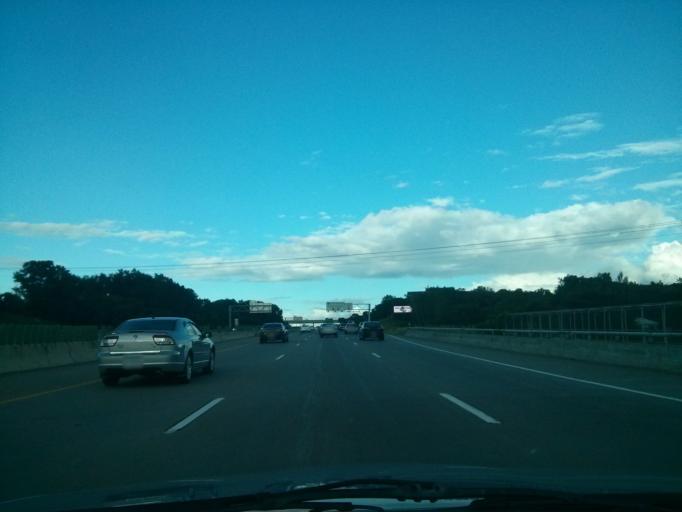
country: US
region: Minnesota
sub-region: Dakota County
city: Mendota Heights
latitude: 44.8611
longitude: -93.1763
